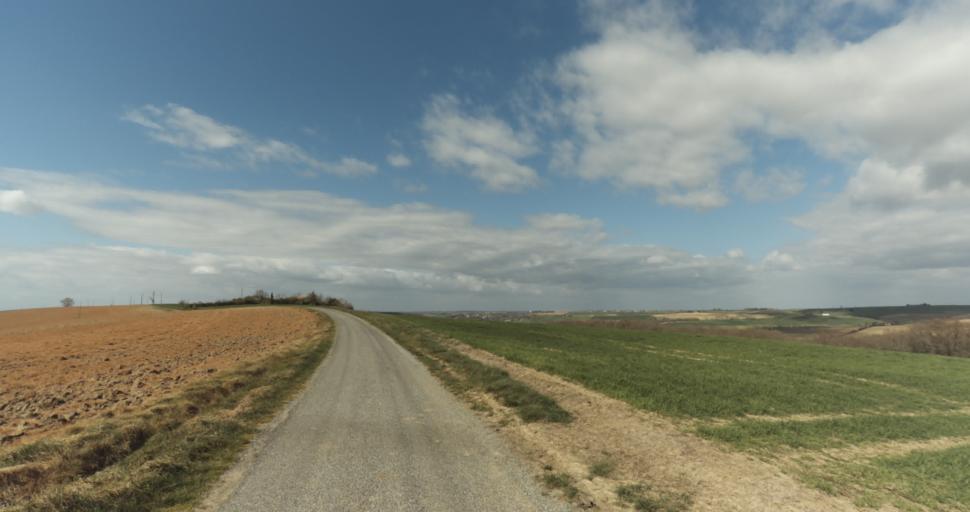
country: FR
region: Midi-Pyrenees
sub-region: Departement de la Haute-Garonne
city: Auterive
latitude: 43.3607
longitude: 1.5144
